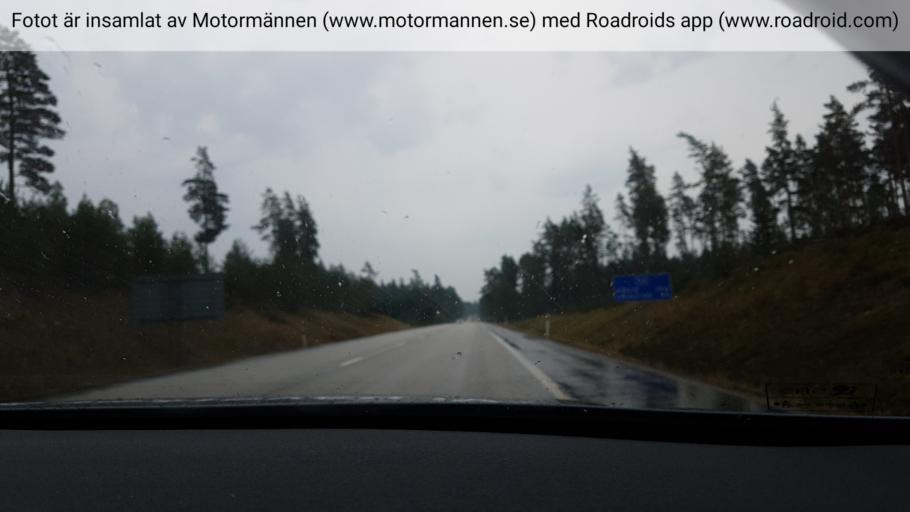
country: SE
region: Joenkoeping
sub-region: Jonkopings Kommun
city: Odensjo
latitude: 57.6142
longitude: 14.2059
